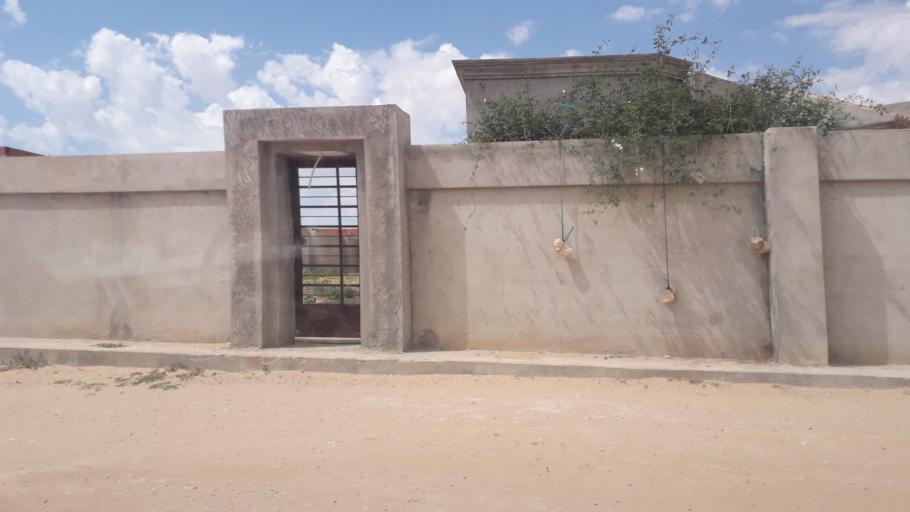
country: TN
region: Safaqis
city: Al Qarmadah
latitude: 34.8395
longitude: 10.7759
